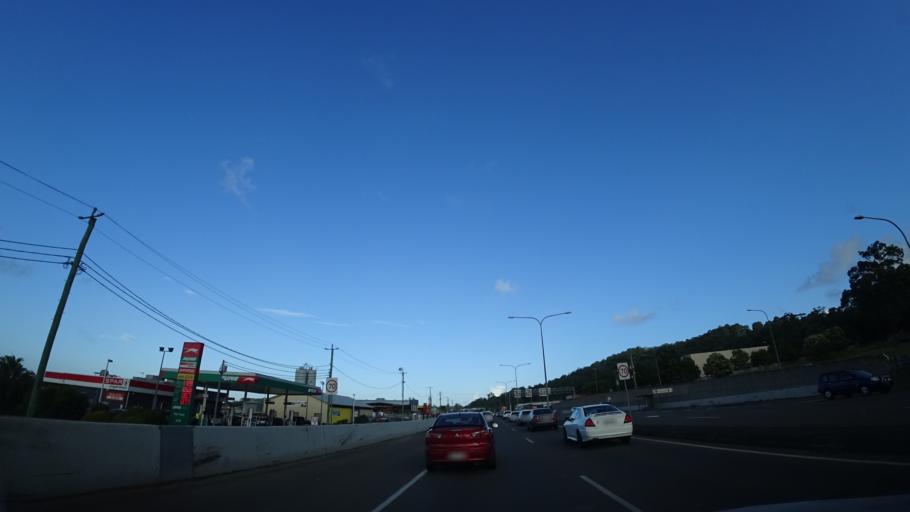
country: AU
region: Queensland
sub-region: Sunshine Coast
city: Buderim
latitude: -26.6625
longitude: 153.0358
